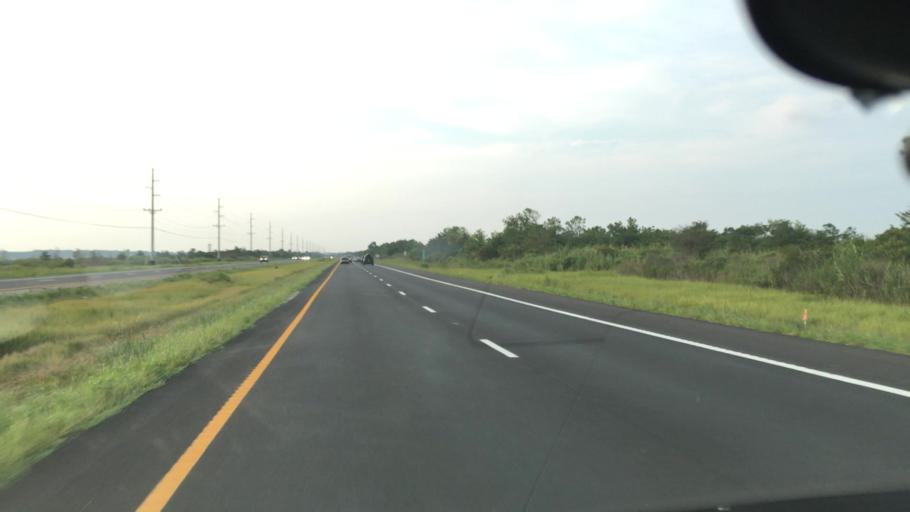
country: US
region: Delaware
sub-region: Sussex County
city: Rehoboth Beach
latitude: 38.6649
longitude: -75.0703
